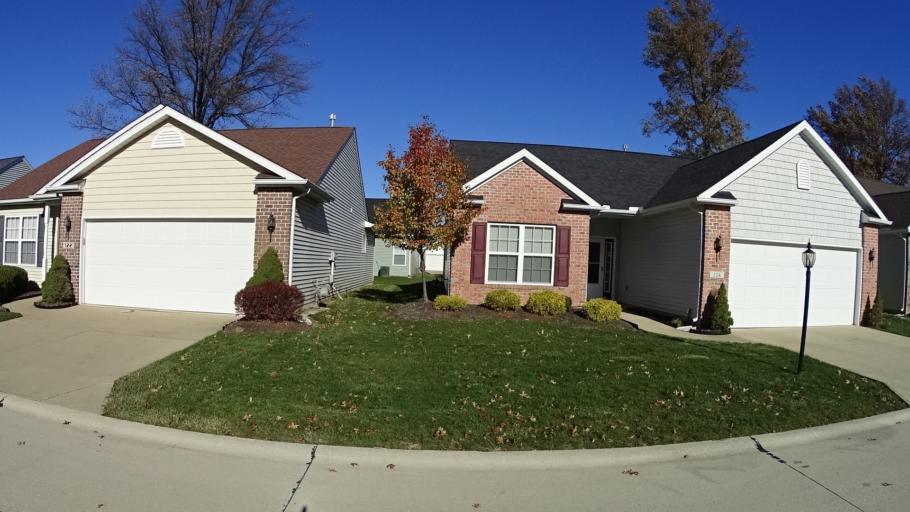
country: US
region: Ohio
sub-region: Lorain County
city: Elyria
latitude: 41.3489
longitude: -82.0704
